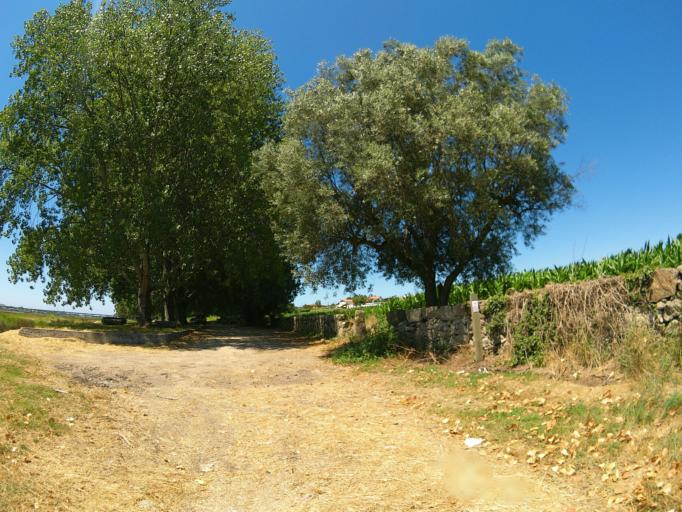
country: PT
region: Viana do Castelo
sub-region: Viana do Castelo
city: Darque
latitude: 41.6989
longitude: -8.7614
